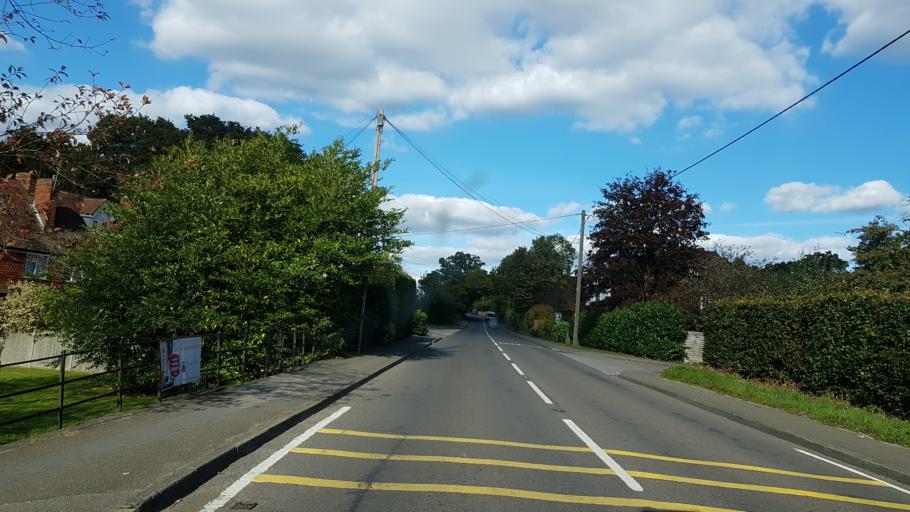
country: GB
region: England
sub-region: Surrey
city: Chiddingfold
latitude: 51.1142
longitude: -0.6275
